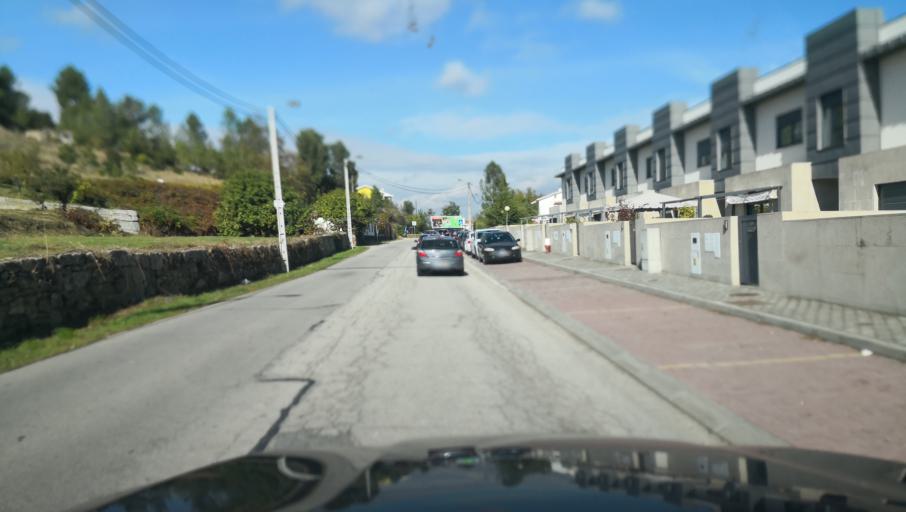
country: PT
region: Vila Real
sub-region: Chaves
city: Chaves
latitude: 41.7340
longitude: -7.4782
